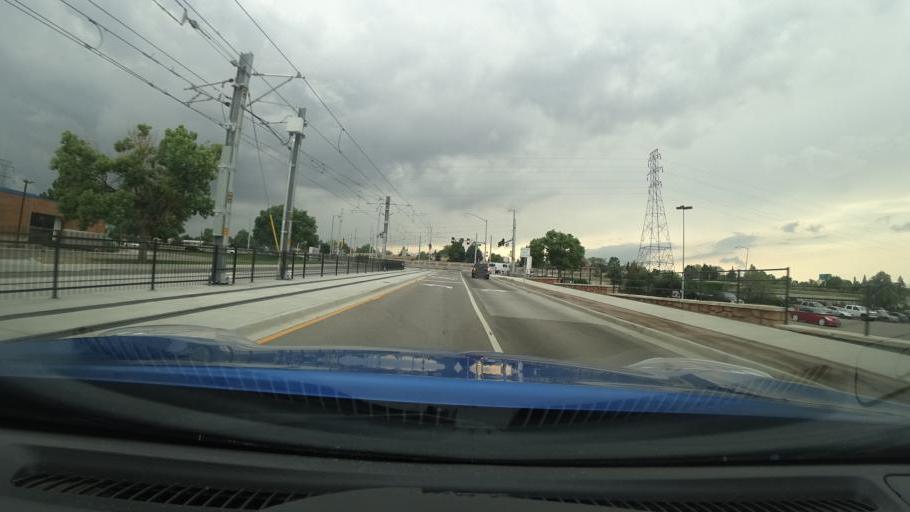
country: US
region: Colorado
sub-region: Adams County
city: Aurora
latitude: 39.7040
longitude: -104.8271
